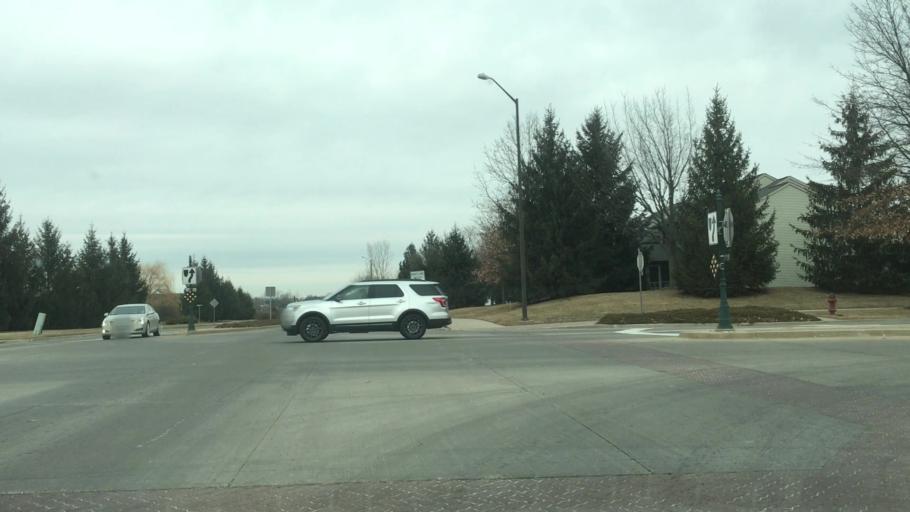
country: US
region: Iowa
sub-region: Johnson County
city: Coralville
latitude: 41.7042
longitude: -91.5878
